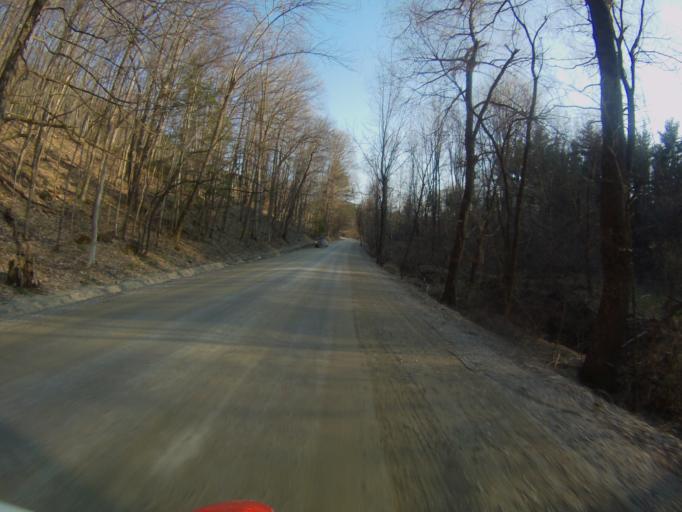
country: US
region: Vermont
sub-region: Addison County
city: Bristol
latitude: 44.0998
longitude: -73.0750
